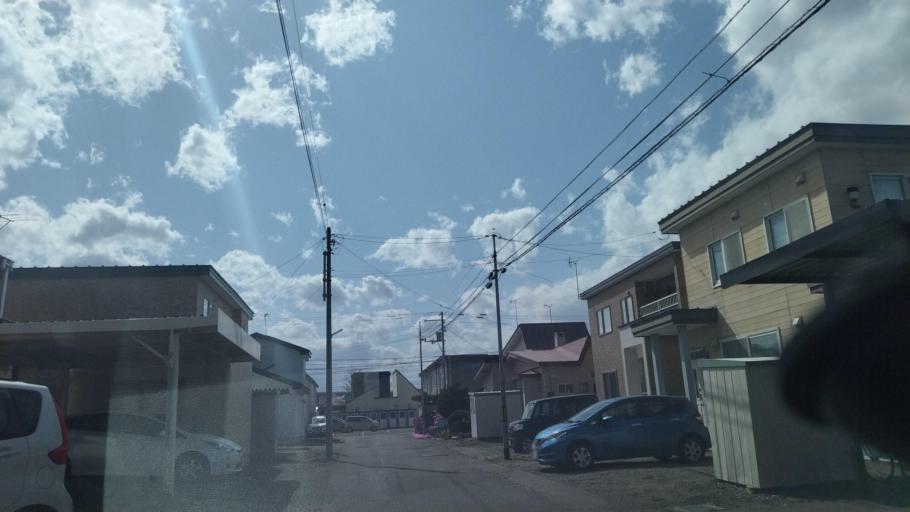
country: JP
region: Hokkaido
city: Obihiro
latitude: 42.9050
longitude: 143.1477
